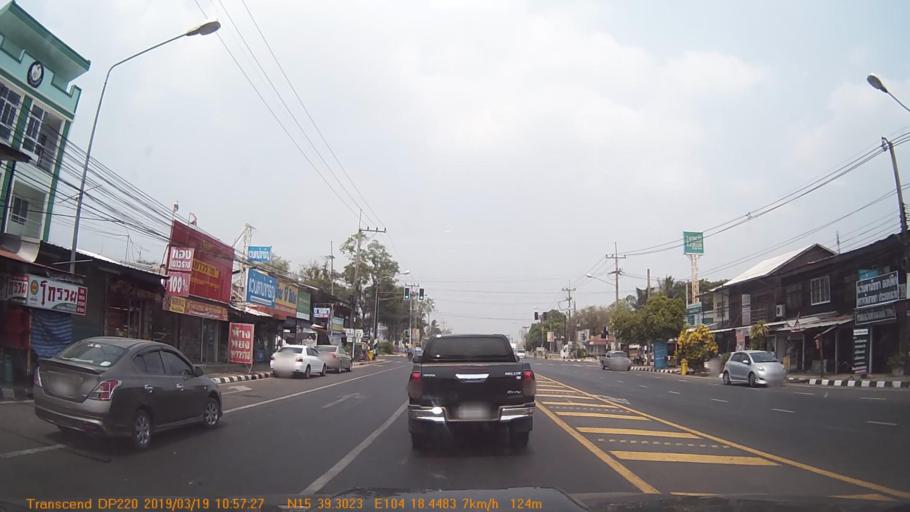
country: TH
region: Yasothon
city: Kham Khuean Kaeo
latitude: 15.6551
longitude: 104.3074
